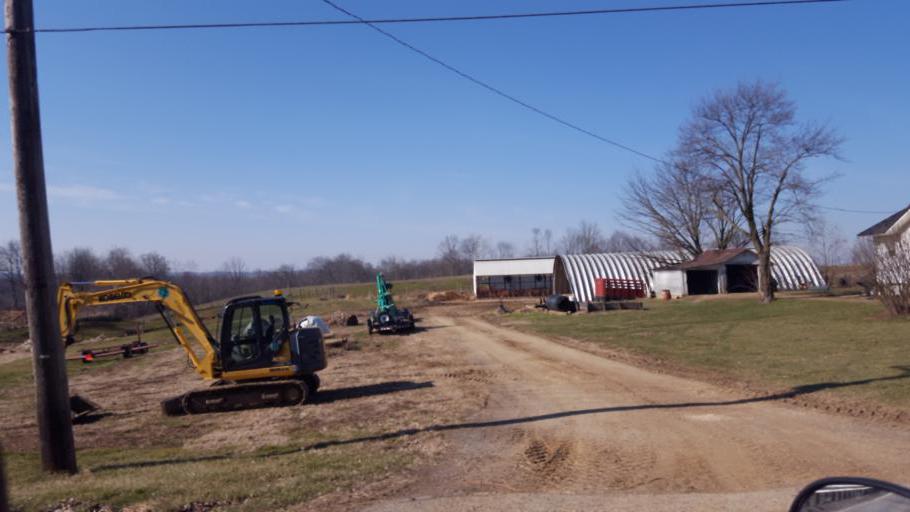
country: US
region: Ohio
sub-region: Wayne County
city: Shreve
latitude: 40.6087
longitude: -82.0244
